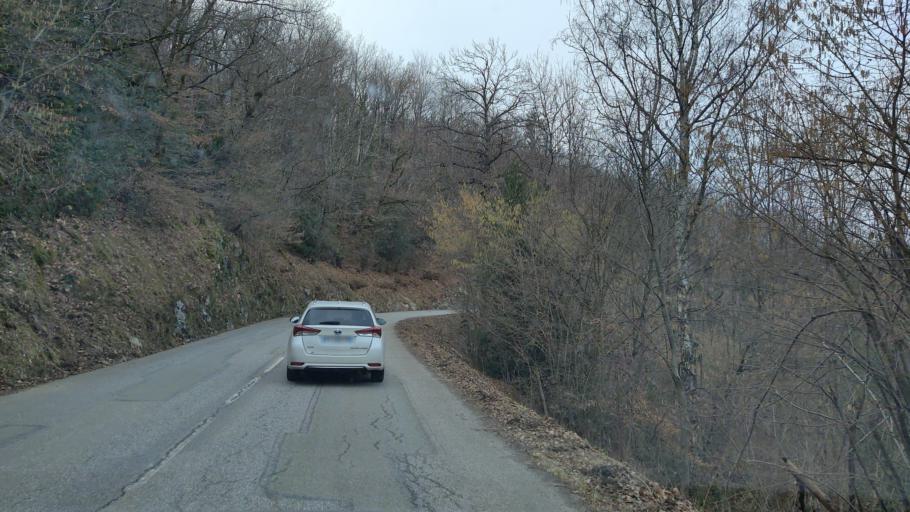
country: FR
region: Rhone-Alpes
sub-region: Departement de la Savoie
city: La Bathie
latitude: 45.6066
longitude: 6.4397
